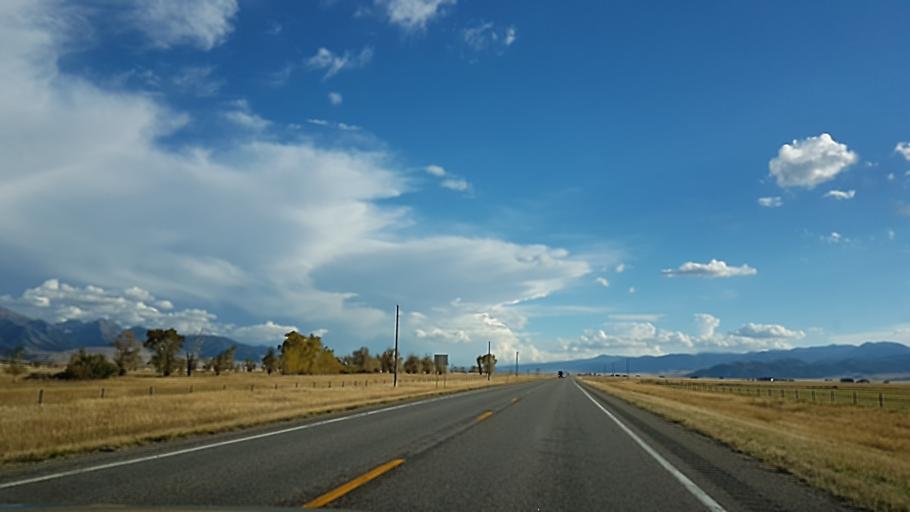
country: US
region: Montana
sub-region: Madison County
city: Virginia City
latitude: 45.1986
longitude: -111.6788
